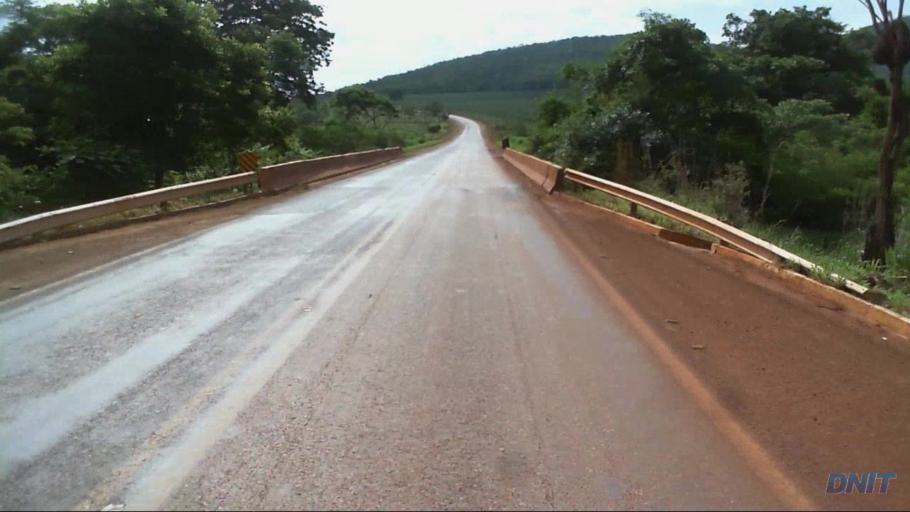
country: BR
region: Goias
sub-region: Barro Alto
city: Barro Alto
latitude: -14.9841
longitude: -48.9248
